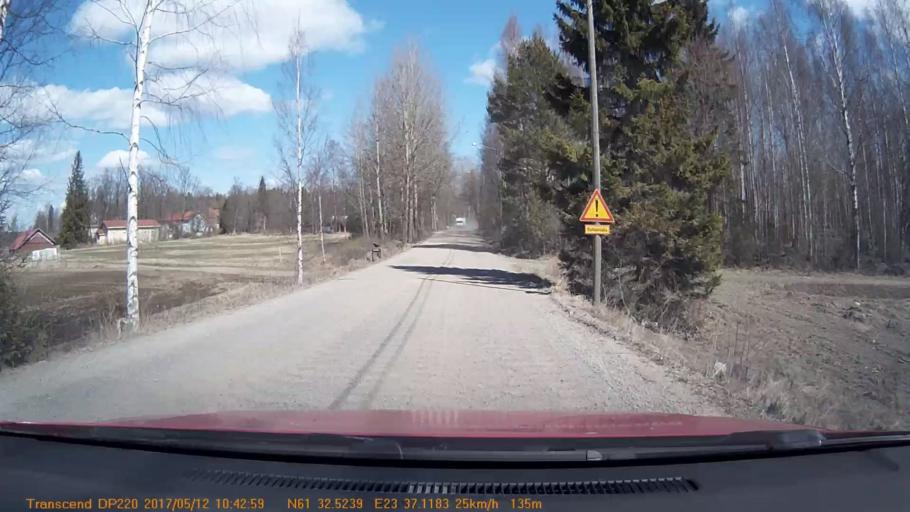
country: FI
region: Pirkanmaa
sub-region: Tampere
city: Yloejaervi
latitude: 61.5420
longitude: 23.6185
